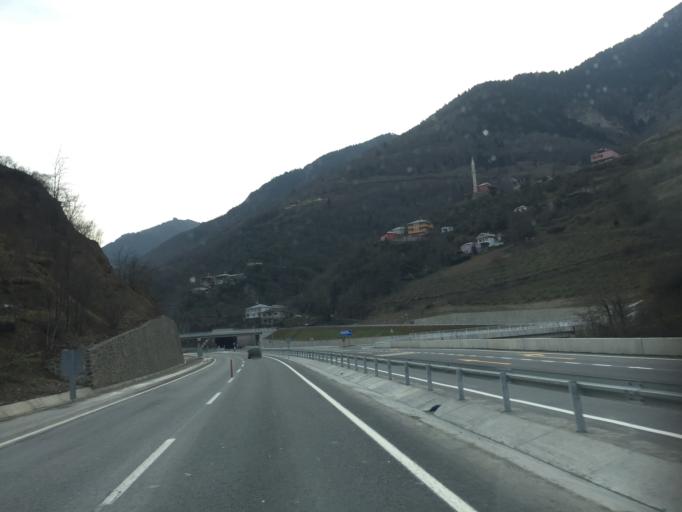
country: TR
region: Trabzon
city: Macka
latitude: 40.7811
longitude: 39.5714
